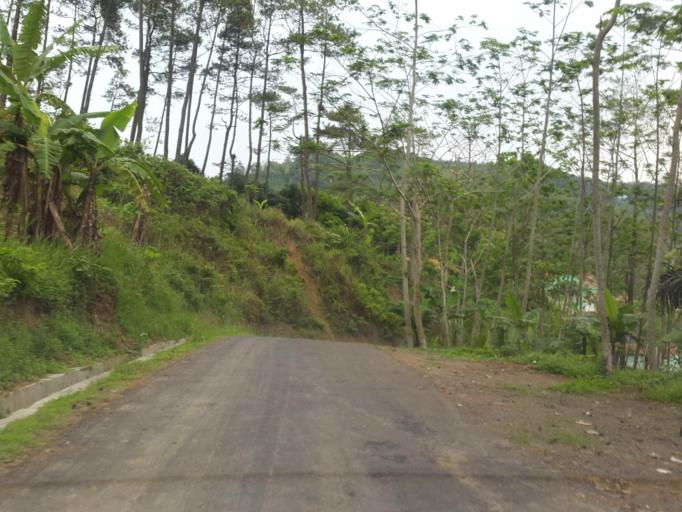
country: ID
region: Central Java
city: Jambuluwuk
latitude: -7.3325
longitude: 108.9259
